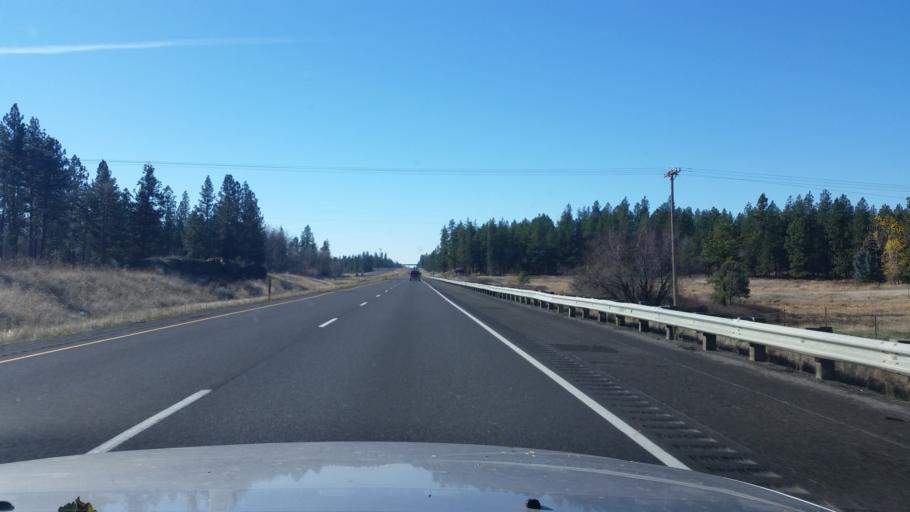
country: US
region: Washington
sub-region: Spokane County
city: Medical Lake
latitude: 47.5132
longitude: -117.6781
